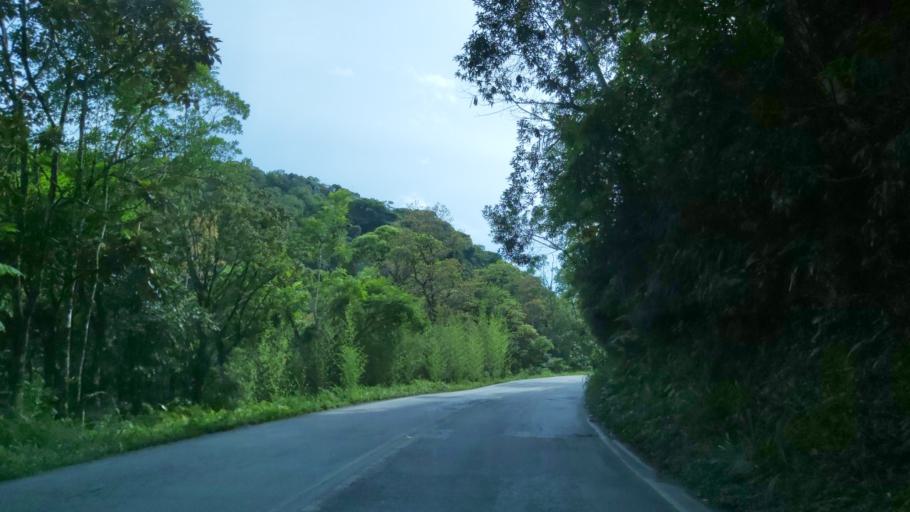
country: BR
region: Sao Paulo
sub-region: Miracatu
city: Miracatu
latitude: -24.0354
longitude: -47.5657
